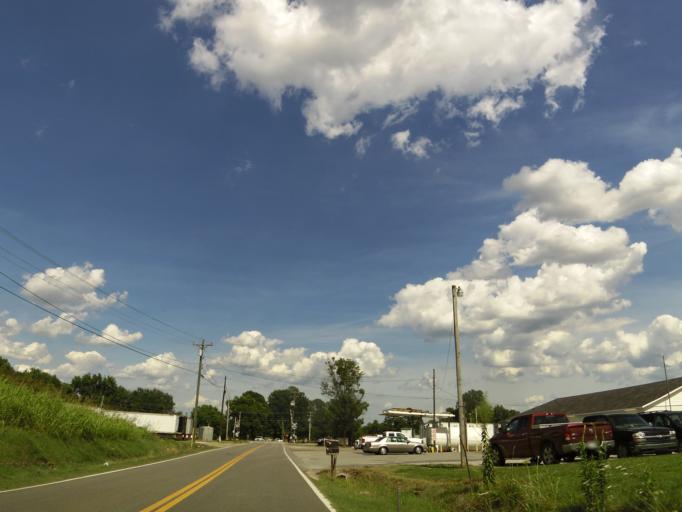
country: US
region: Tennessee
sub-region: Gibson County
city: Milan
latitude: 35.9759
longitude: -88.7852
